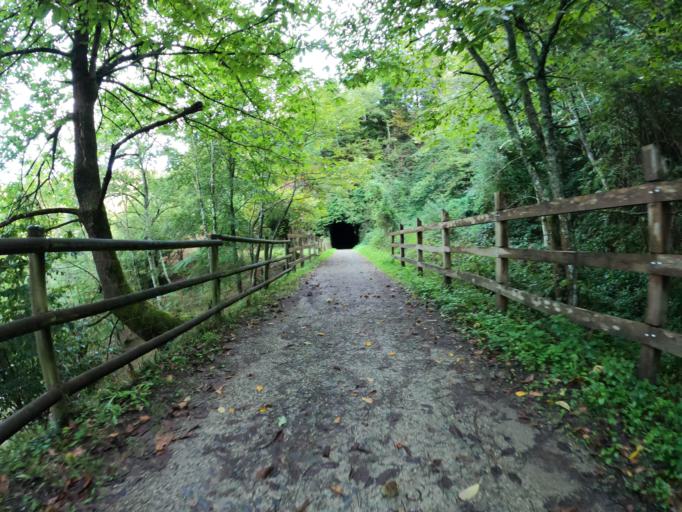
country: ES
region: Navarre
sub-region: Provincia de Navarra
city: Leitza
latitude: 43.0830
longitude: -1.9031
